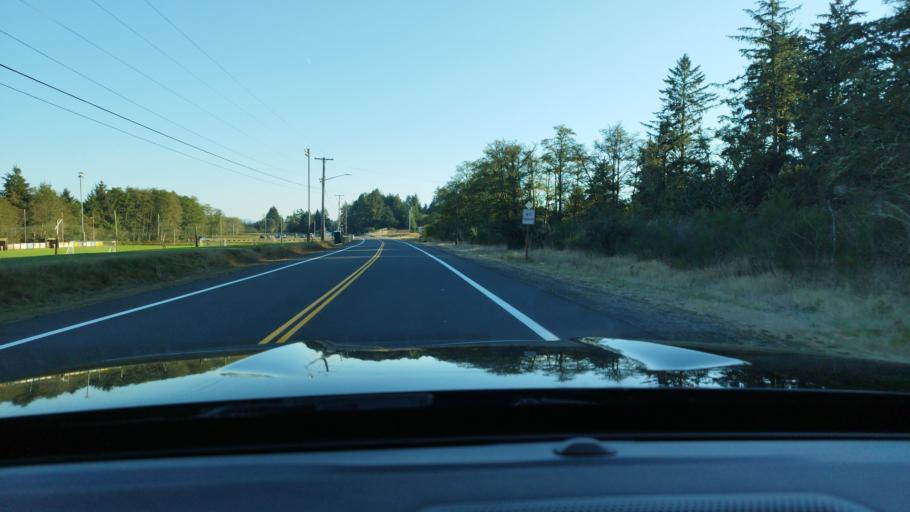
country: US
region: Oregon
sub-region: Clatsop County
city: Warrenton
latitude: 46.1656
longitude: -123.9488
